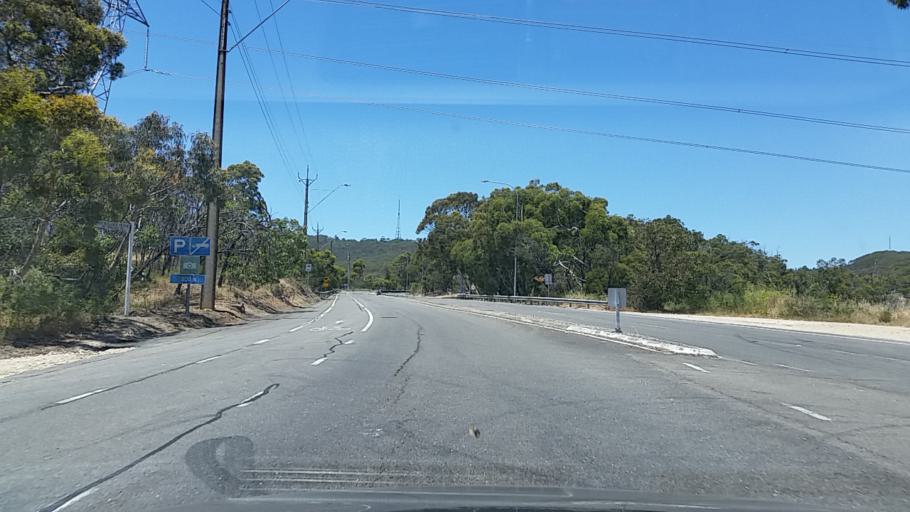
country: AU
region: South Australia
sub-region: Burnside
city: Mount Osmond
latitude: -34.9760
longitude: 138.6820
